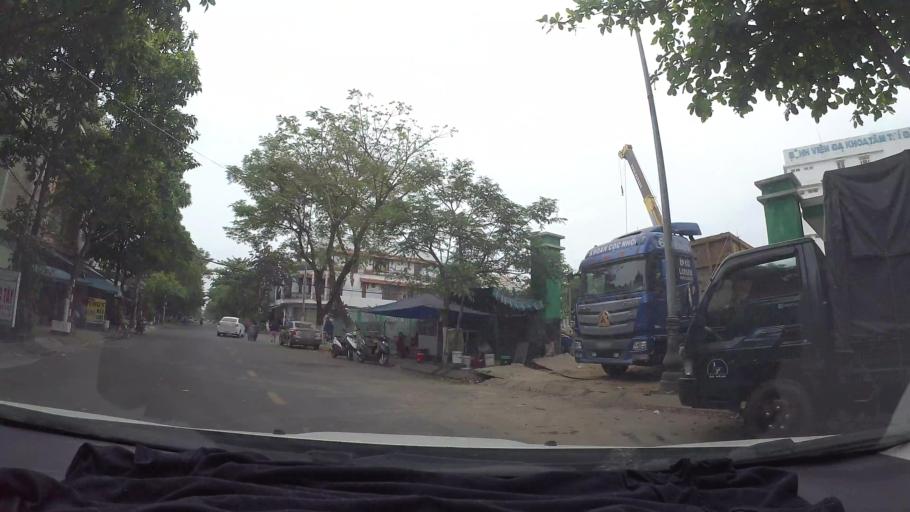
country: VN
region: Da Nang
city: Cam Le
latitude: 16.0225
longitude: 108.2133
